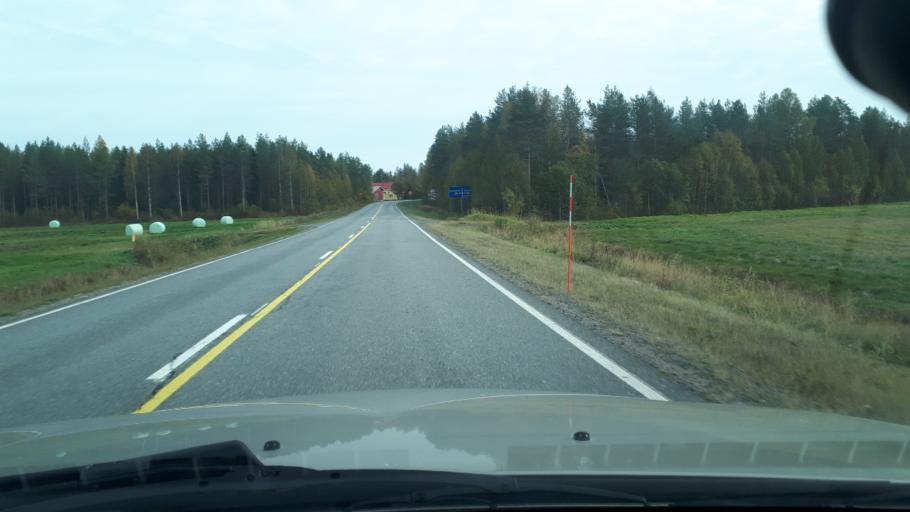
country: FI
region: Lapland
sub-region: Rovaniemi
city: Ranua
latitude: 66.0121
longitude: 26.3091
